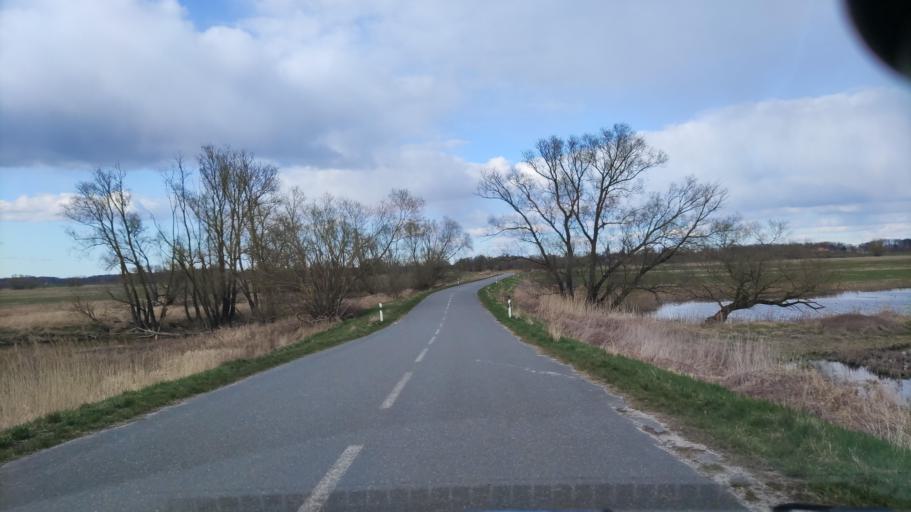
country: DE
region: Mecklenburg-Vorpommern
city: Domitz
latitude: 53.1321
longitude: 11.2367
